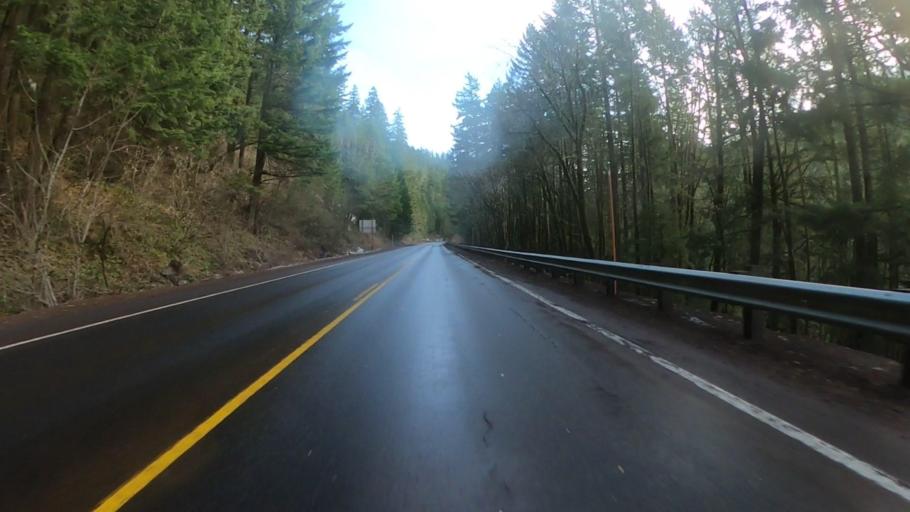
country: US
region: Oregon
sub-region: Lane County
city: Oakridge
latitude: 43.6410
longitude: -122.1792
